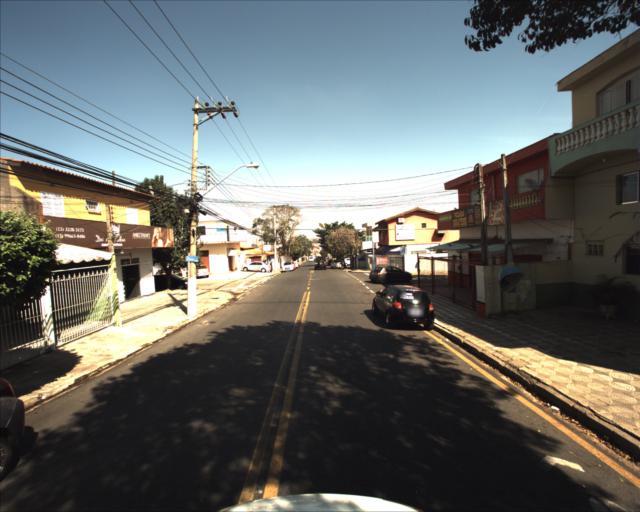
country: BR
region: Sao Paulo
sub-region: Sorocaba
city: Sorocaba
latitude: -23.4707
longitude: -47.4368
